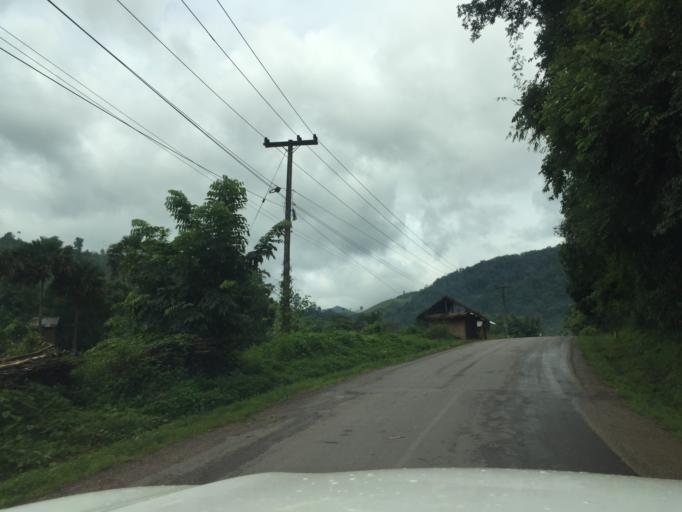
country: LA
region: Oudomxai
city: Muang La
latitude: 20.7872
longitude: 102.0765
